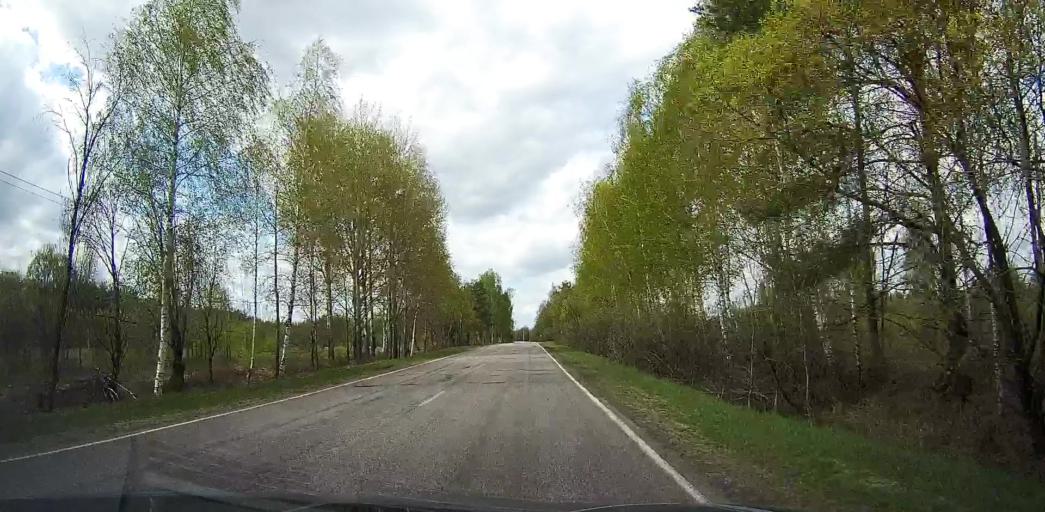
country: RU
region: Moskovskaya
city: Davydovo
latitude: 55.6604
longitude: 38.8101
